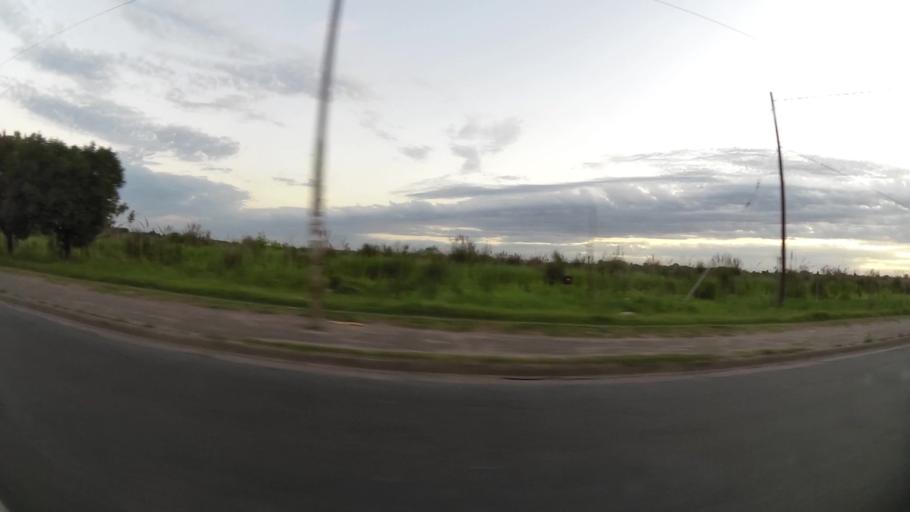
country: AR
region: Buenos Aires
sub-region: Partido de Merlo
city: Merlo
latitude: -34.6696
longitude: -58.7453
